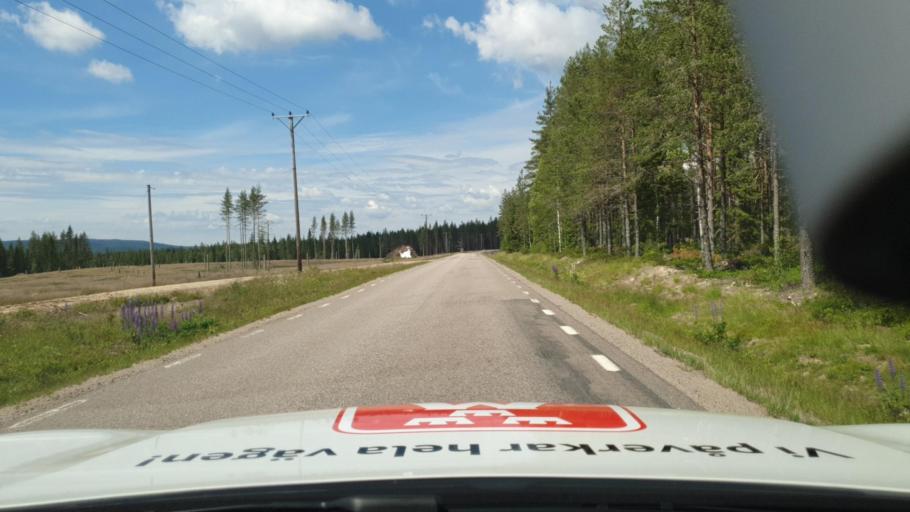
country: SE
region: Vaermland
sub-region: Torsby Kommun
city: Torsby
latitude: 60.4979
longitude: 12.8615
